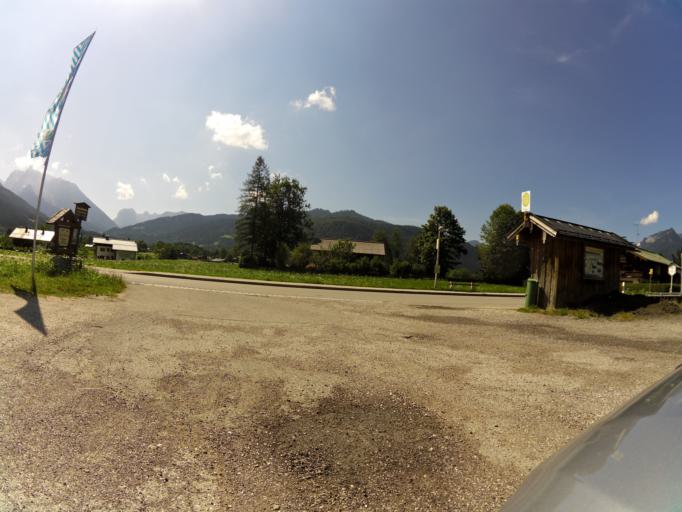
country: DE
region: Bavaria
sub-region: Upper Bavaria
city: Schoenau am Koenigssee
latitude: 47.6145
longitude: 12.9818
